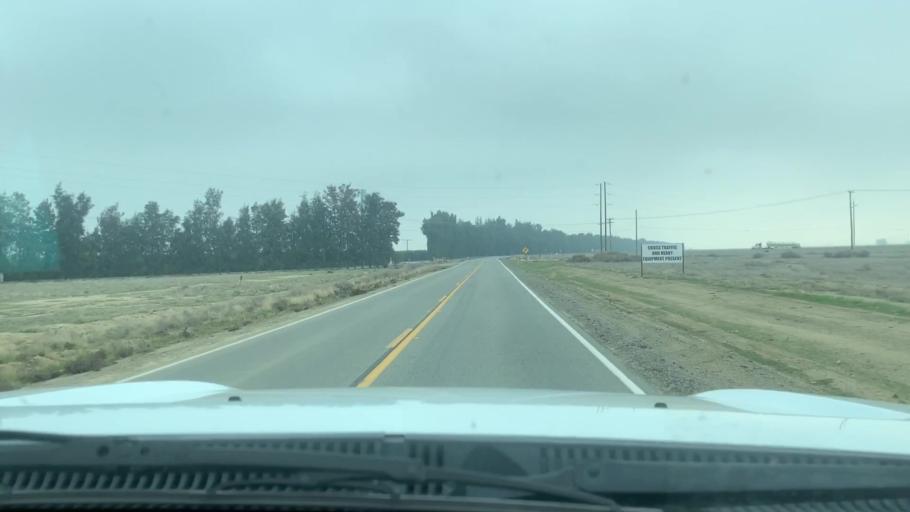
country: US
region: California
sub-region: Kern County
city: Lost Hills
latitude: 35.5295
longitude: -119.7626
